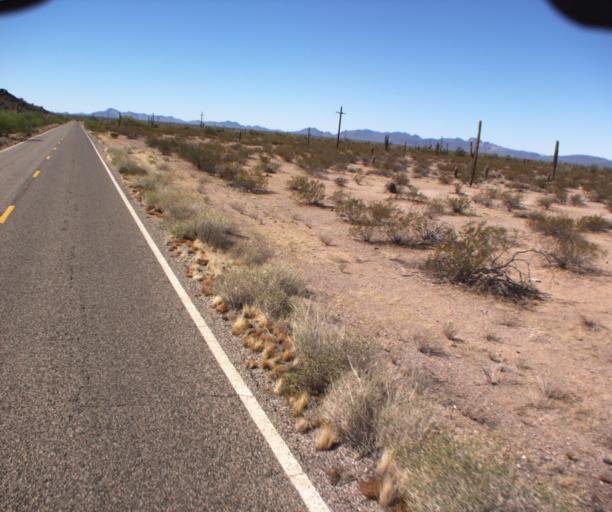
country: US
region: Arizona
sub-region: Pima County
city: Ajo
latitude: 32.2344
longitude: -112.7521
